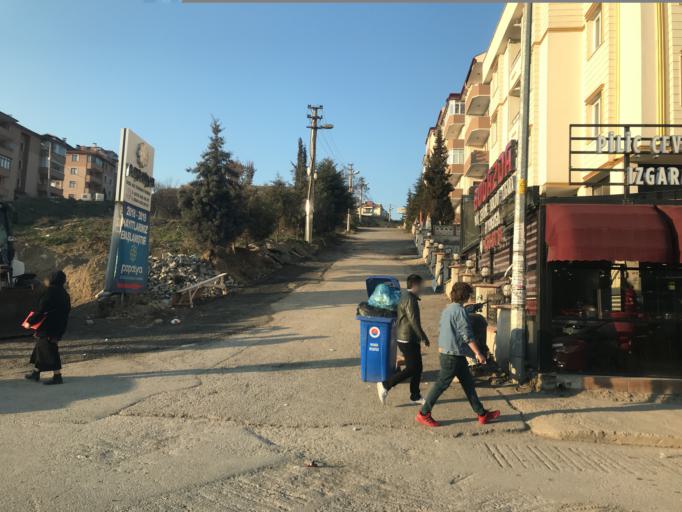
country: TR
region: Karabuk
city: Karabuk
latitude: 41.2182
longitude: 32.6657
